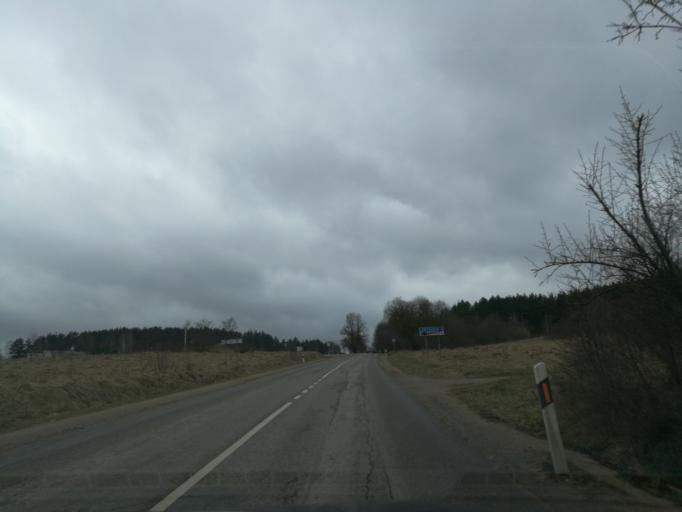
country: LT
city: Grigiskes
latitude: 54.6476
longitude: 25.1141
